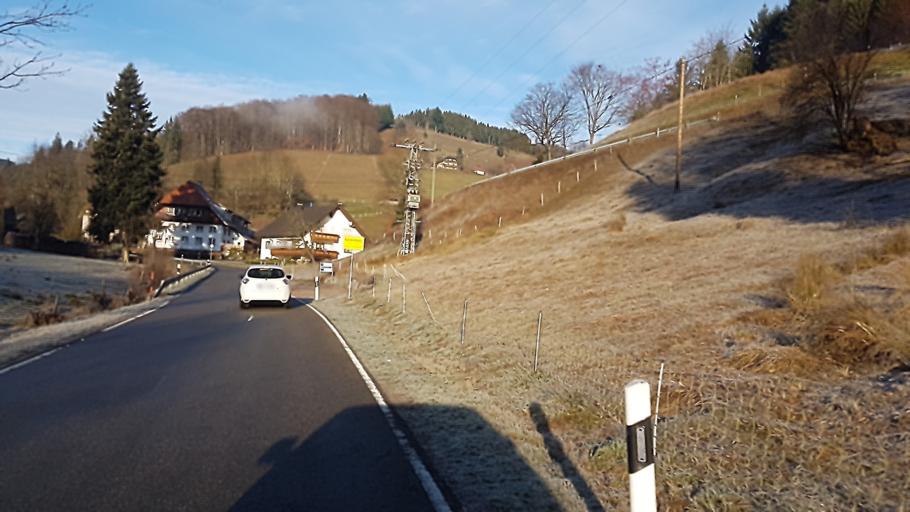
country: DE
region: Baden-Wuerttemberg
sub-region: Freiburg Region
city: Elzach
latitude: 48.1626
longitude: 8.0220
